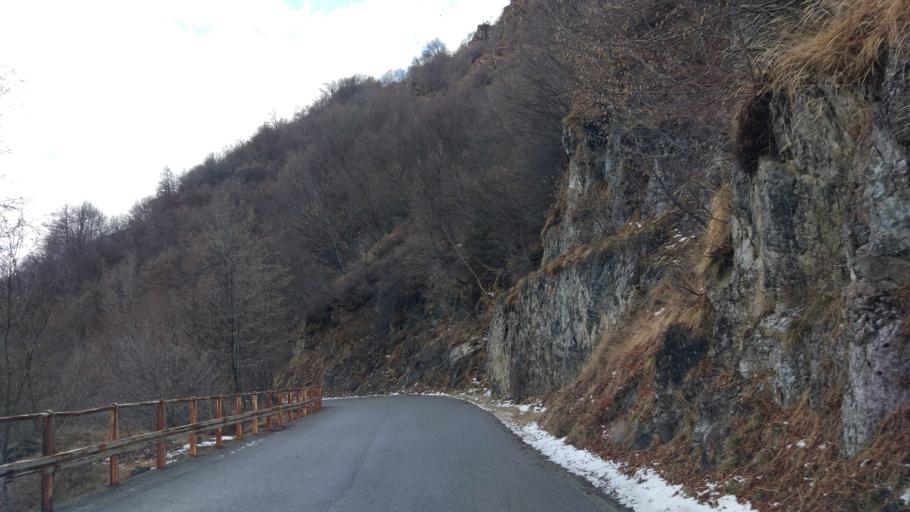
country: IT
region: Lombardy
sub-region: Provincia di Lecco
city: Moggio
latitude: 45.9158
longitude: 9.4936
